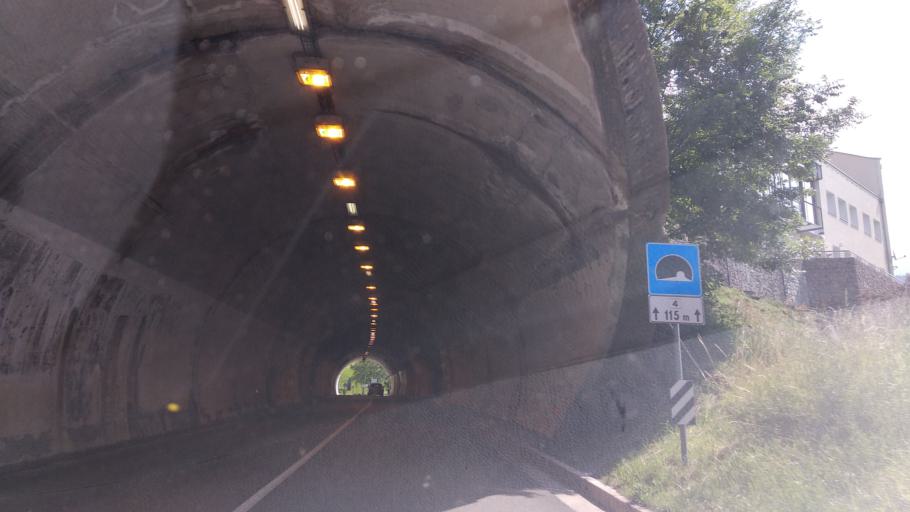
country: IT
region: Trentino-Alto Adige
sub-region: Bolzano
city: Avelengo
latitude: 46.6475
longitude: 11.2171
